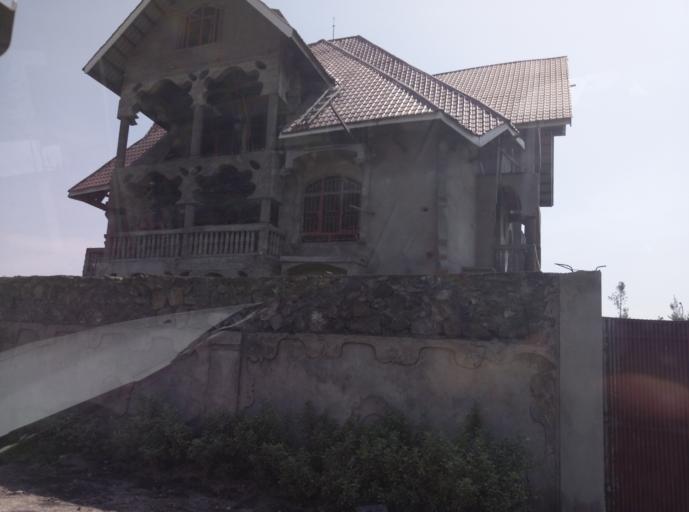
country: CD
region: Nord Kivu
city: Goma
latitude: -1.6339
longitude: 29.1688
